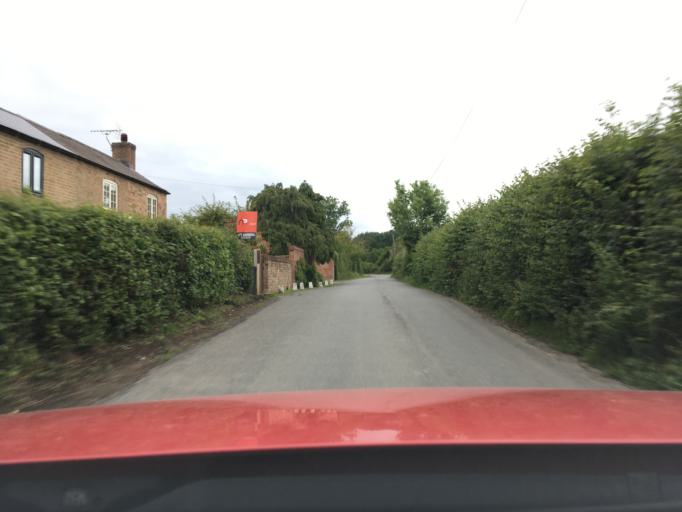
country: GB
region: England
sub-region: Gloucestershire
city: Stonehouse
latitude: 51.7870
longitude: -2.3795
